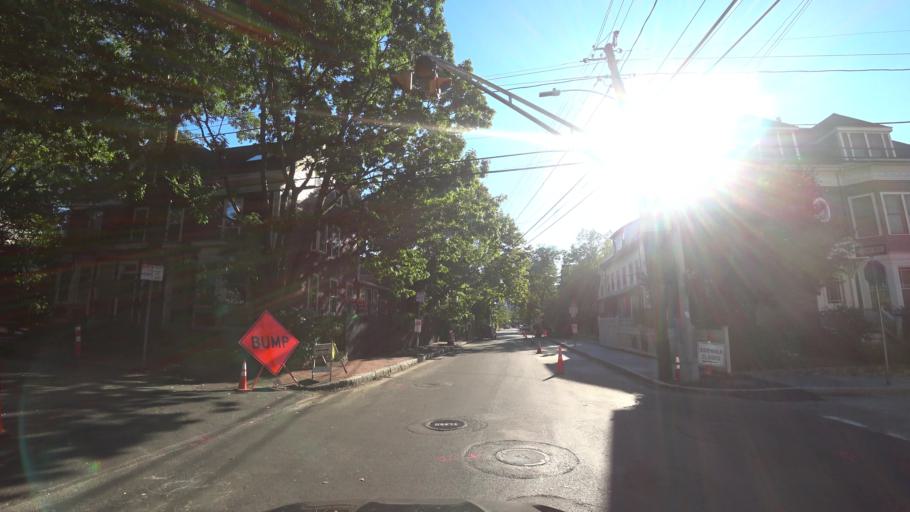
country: US
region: Massachusetts
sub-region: Middlesex County
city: Cambridge
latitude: 42.3577
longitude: -71.1102
